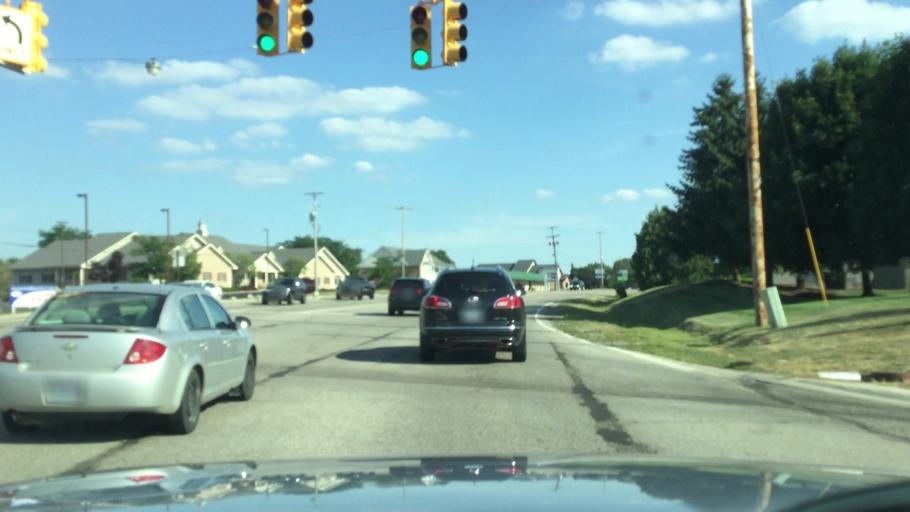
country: US
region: Michigan
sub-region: Genesee County
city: Grand Blanc
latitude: 42.9090
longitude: -83.6045
